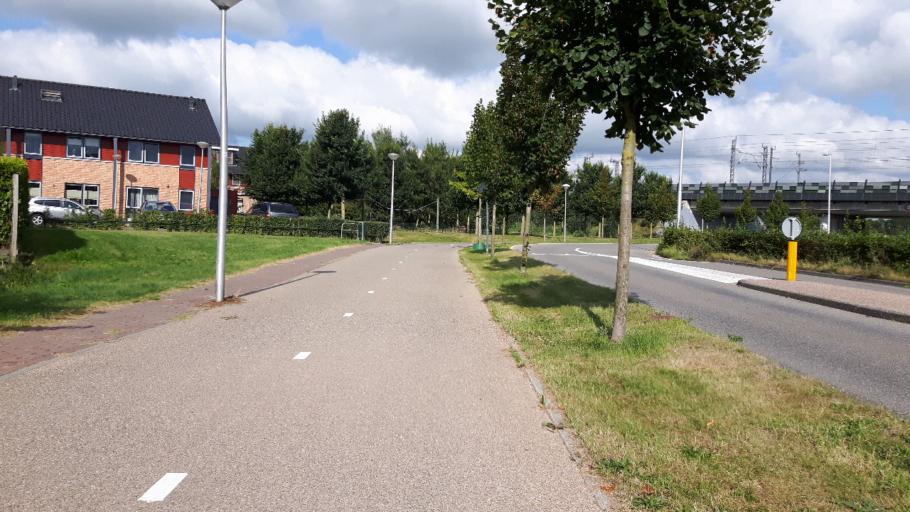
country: NL
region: Utrecht
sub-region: Stichtse Vecht
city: Spechtenkamp
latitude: 52.1025
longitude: 5.0002
